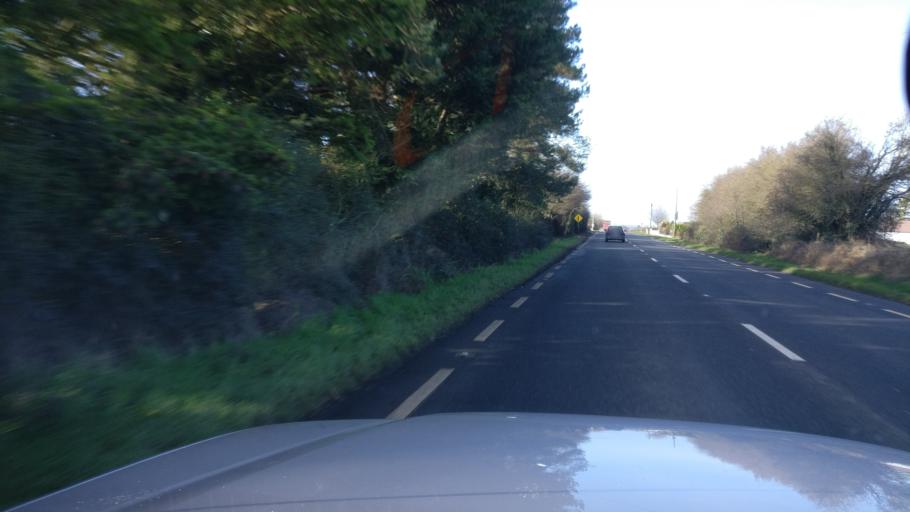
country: IE
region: Leinster
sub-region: Uibh Fhaili
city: Tullamore
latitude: 53.2083
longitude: -7.4374
